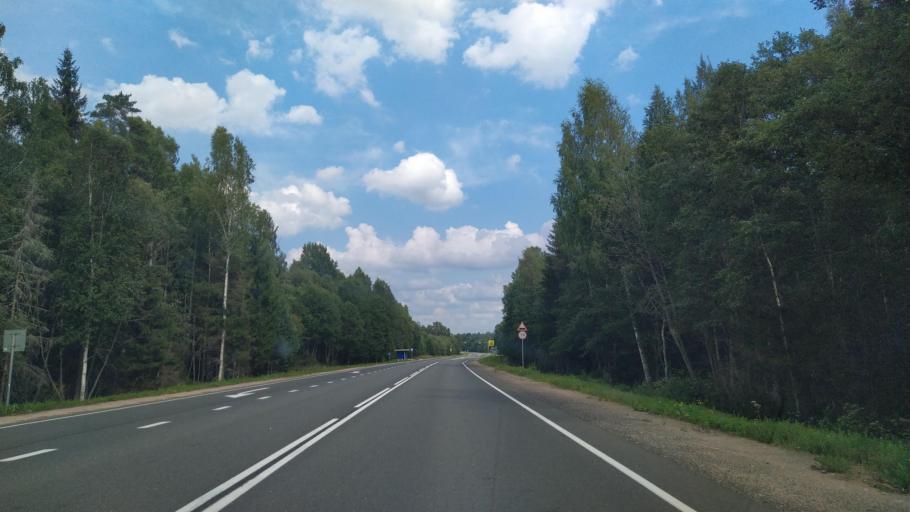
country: RU
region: Pskov
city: Dno
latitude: 57.9927
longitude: 29.8403
